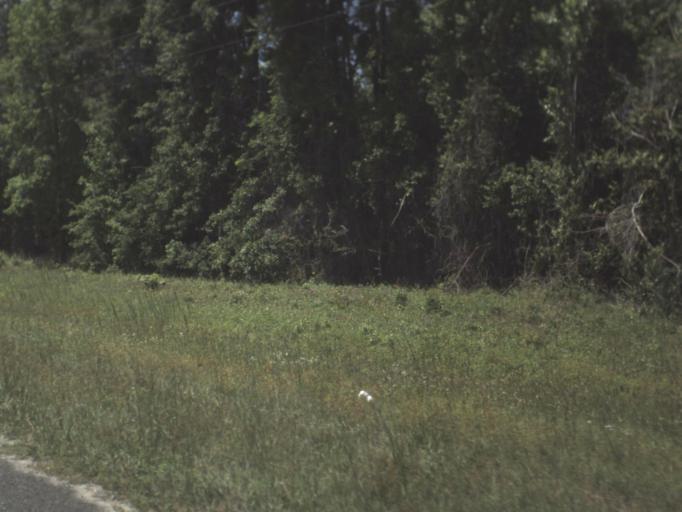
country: US
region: Florida
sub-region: Jefferson County
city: Monticello
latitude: 30.4659
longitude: -83.8920
